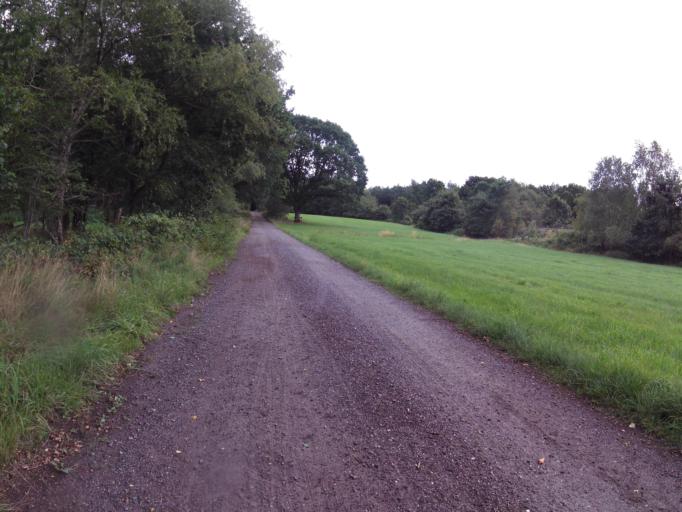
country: DE
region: Lower Saxony
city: Hipstedt
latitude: 53.5005
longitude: 8.9352
